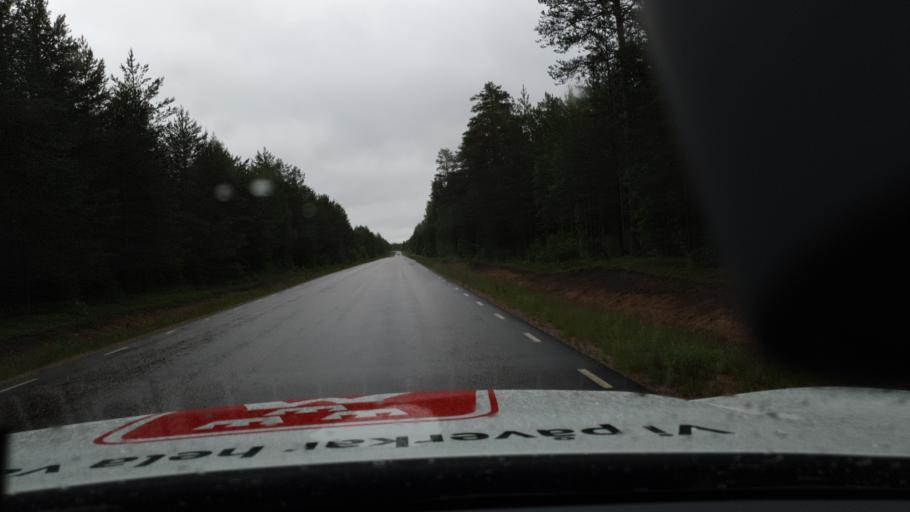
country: SE
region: Norrbotten
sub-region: Overtornea Kommun
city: OEvertornea
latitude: 66.4729
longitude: 23.6767
